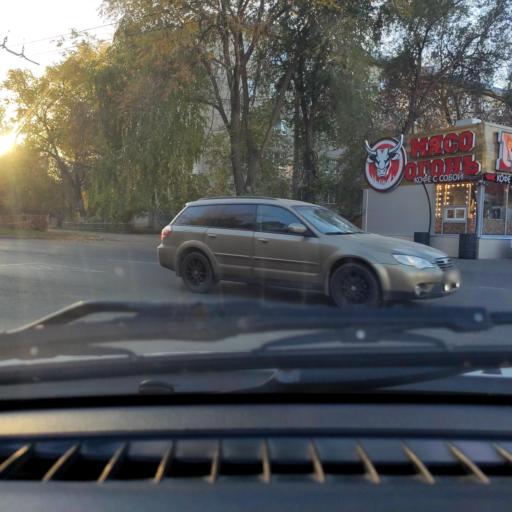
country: RU
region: Samara
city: Tol'yatti
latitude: 53.5221
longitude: 49.4207
